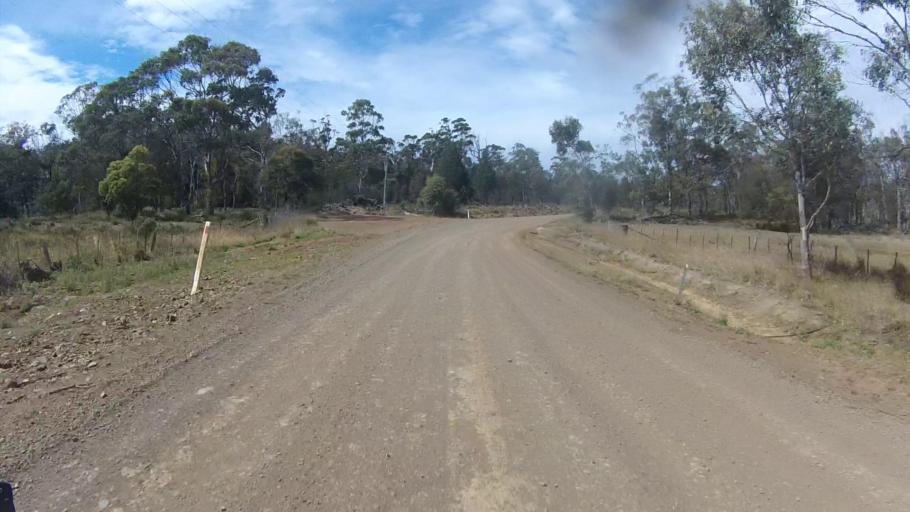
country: AU
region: Tasmania
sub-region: Sorell
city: Sorell
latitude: -42.6479
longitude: 147.8995
